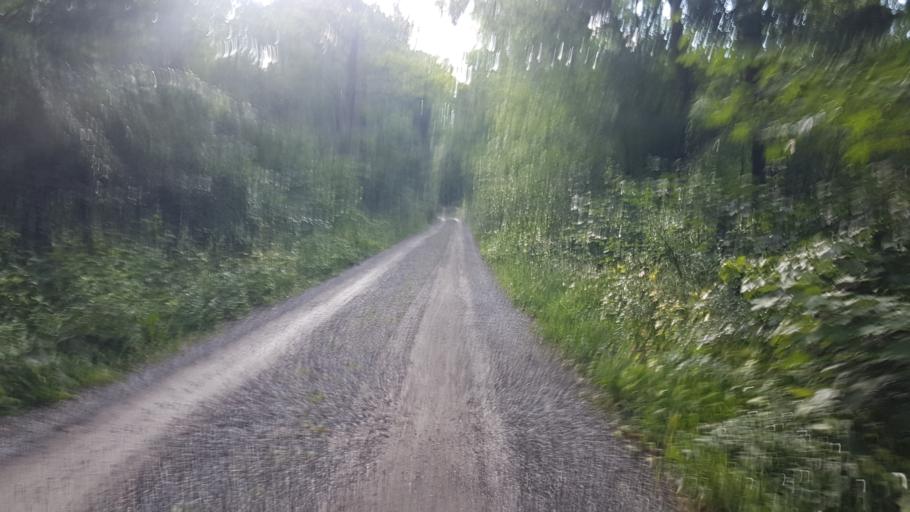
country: DE
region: Baden-Wuerttemberg
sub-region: Regierungsbezirk Stuttgart
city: Zaberfeld
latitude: 49.0376
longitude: 8.9197
